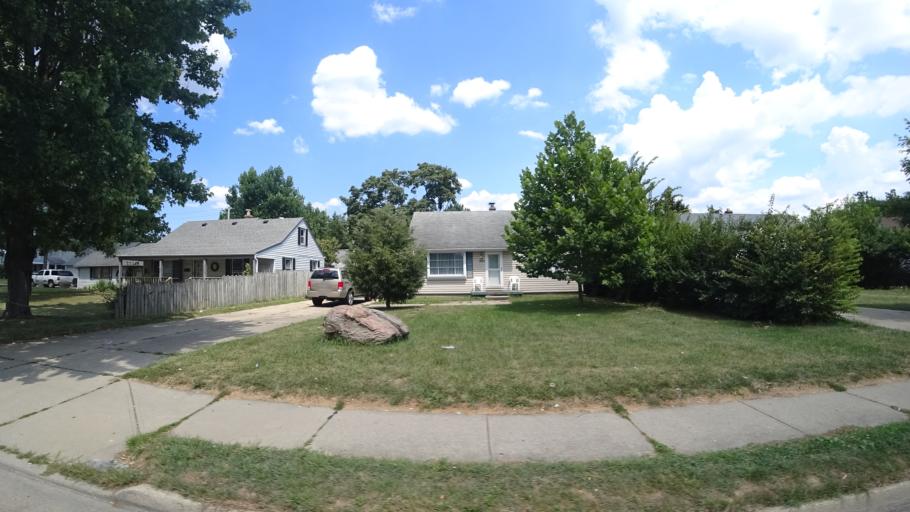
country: US
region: Ohio
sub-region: Butler County
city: Hamilton
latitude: 39.4190
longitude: -84.5882
